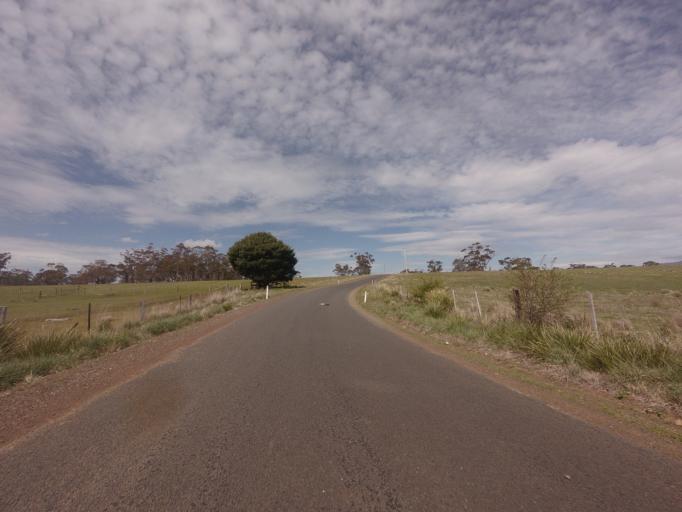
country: AU
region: Tasmania
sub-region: Northern Midlands
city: Longford
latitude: -41.7727
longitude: 147.2217
